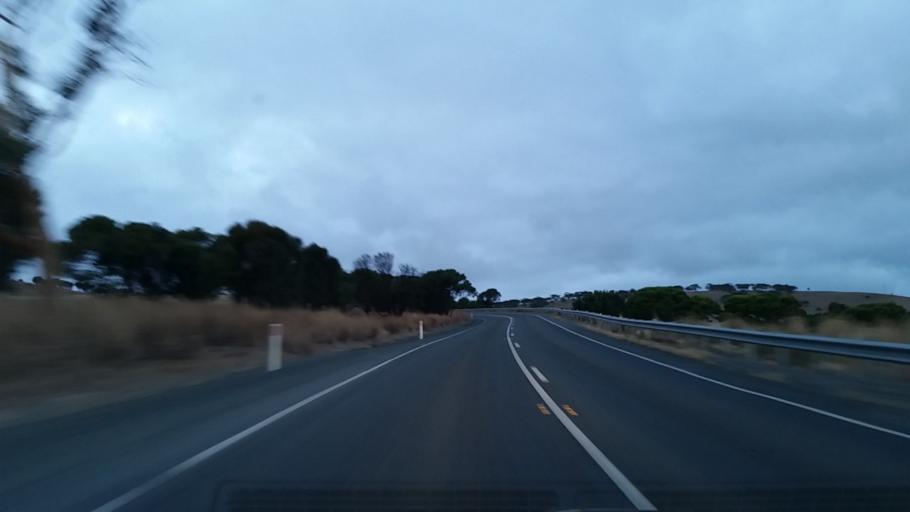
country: AU
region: South Australia
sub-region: Yankalilla
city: Normanville
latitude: -35.6060
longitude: 138.1338
